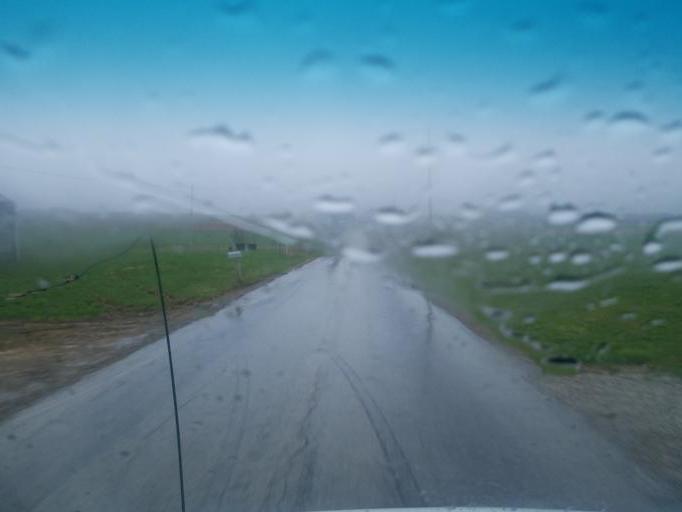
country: US
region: Ohio
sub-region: Knox County
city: Oak Hill
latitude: 40.4856
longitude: -82.1284
